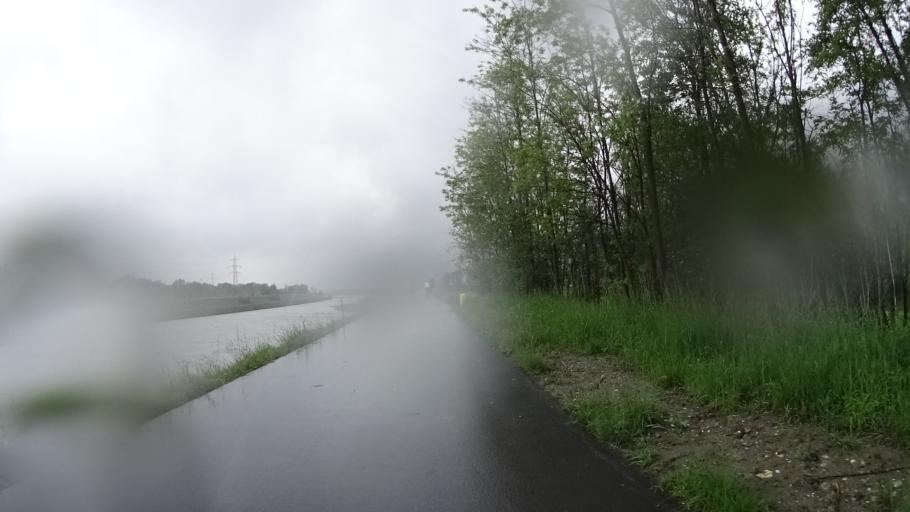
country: LI
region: Triesen
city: Triesen
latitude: 47.0892
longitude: 9.5173
